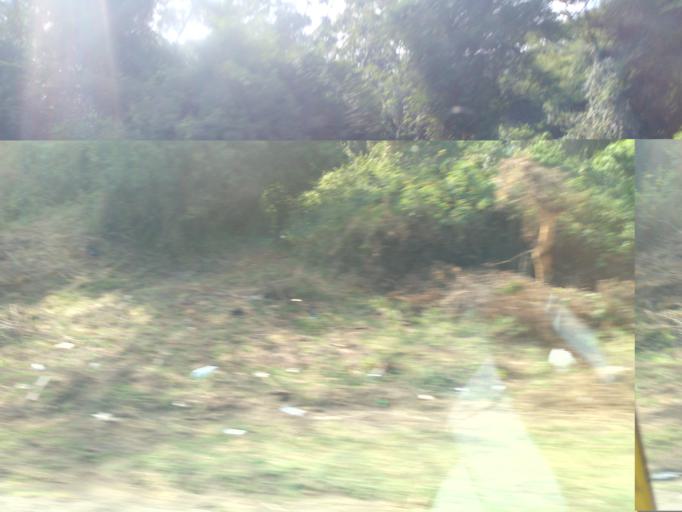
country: KE
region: Kiambu
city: Limuru
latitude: -1.0331
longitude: 36.6019
